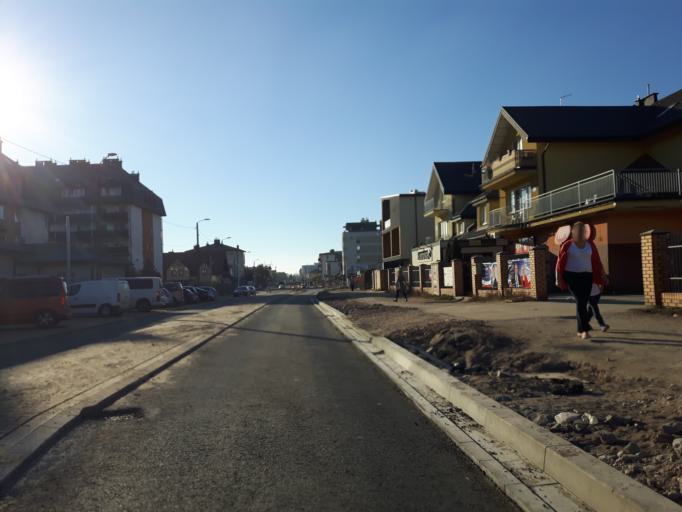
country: PL
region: Masovian Voivodeship
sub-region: Powiat wolominski
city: Zabki
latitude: 52.2801
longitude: 21.1331
